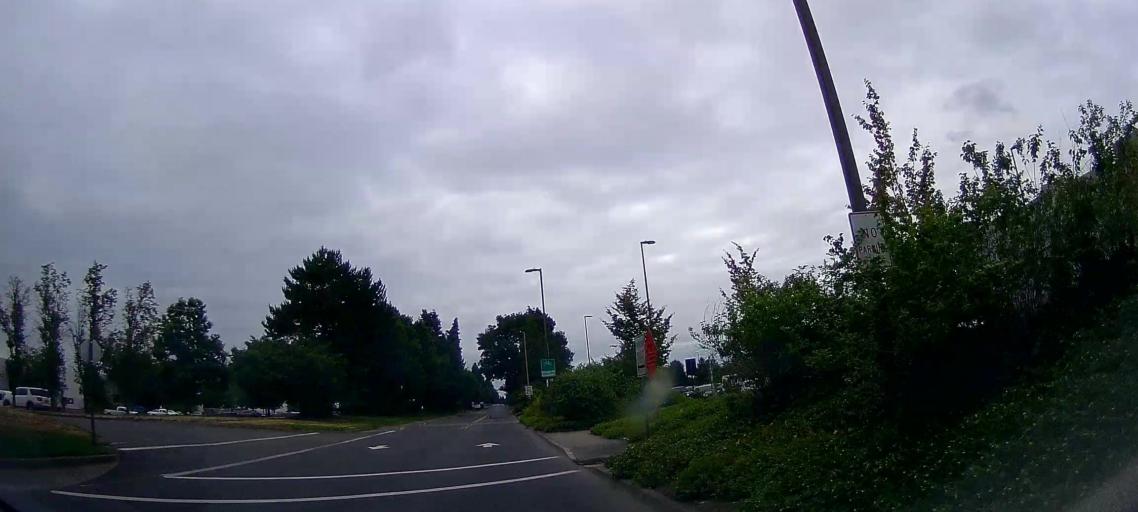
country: US
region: Washington
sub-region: Clark County
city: Orchards
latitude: 45.5814
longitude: -122.5725
